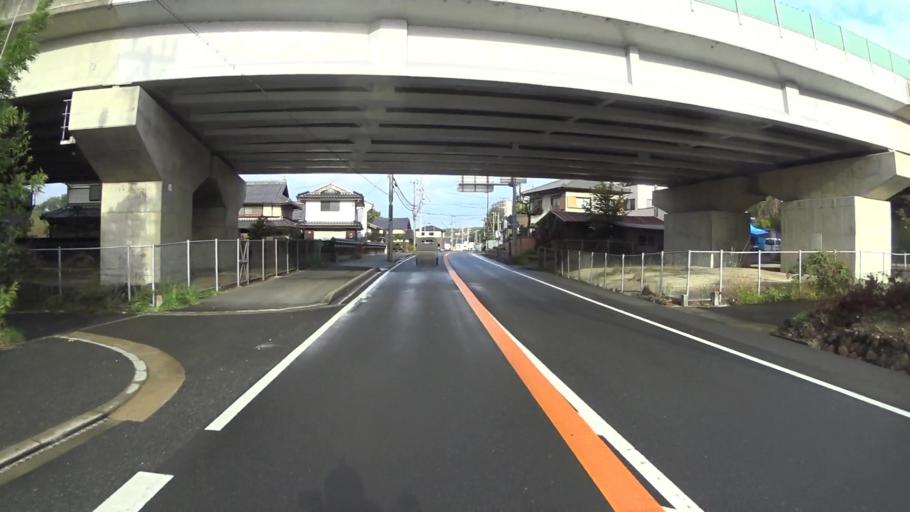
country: JP
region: Kyoto
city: Ayabe
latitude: 35.2648
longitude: 135.1851
